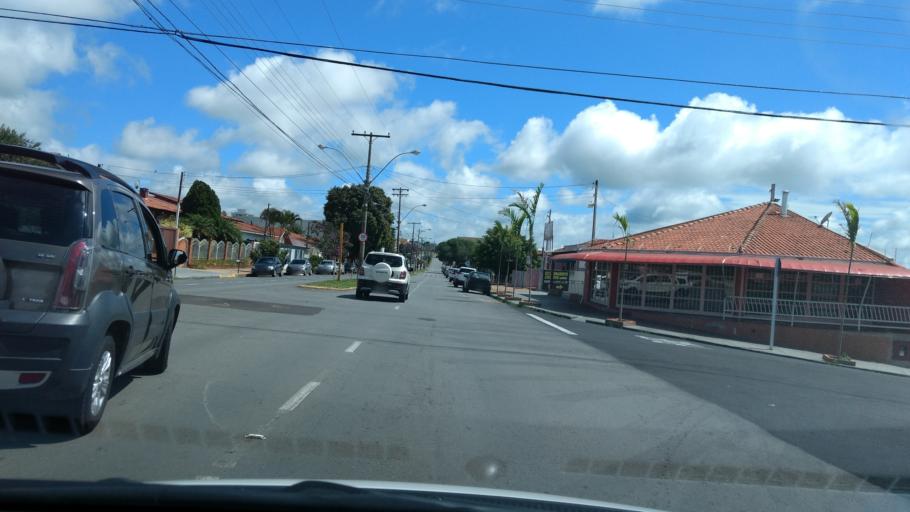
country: BR
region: Sao Paulo
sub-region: Botucatu
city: Botucatu
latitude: -22.8648
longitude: -48.4426
